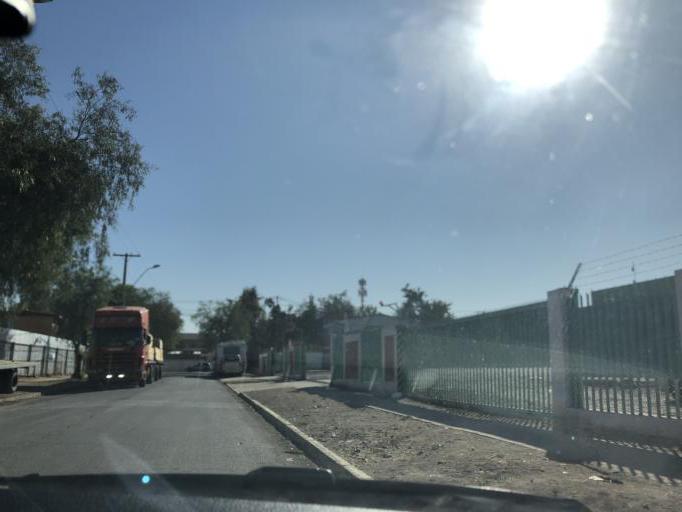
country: CL
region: Santiago Metropolitan
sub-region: Provincia de Cordillera
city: Puente Alto
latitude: -33.6177
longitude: -70.6111
